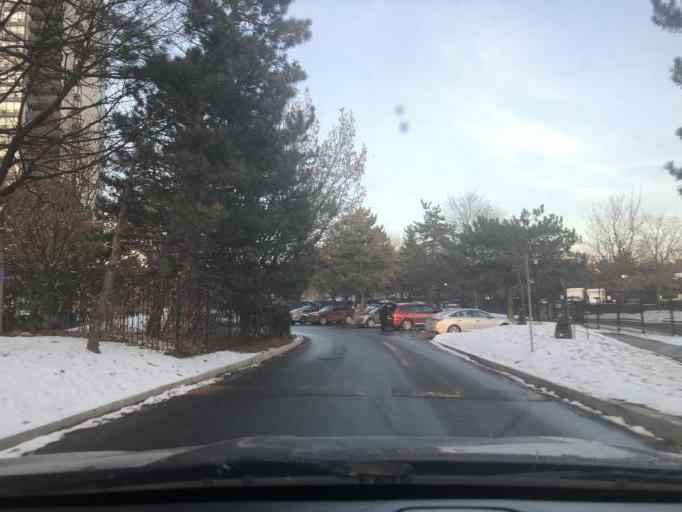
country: CA
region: Ontario
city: Toronto
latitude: 43.6970
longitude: -79.4894
